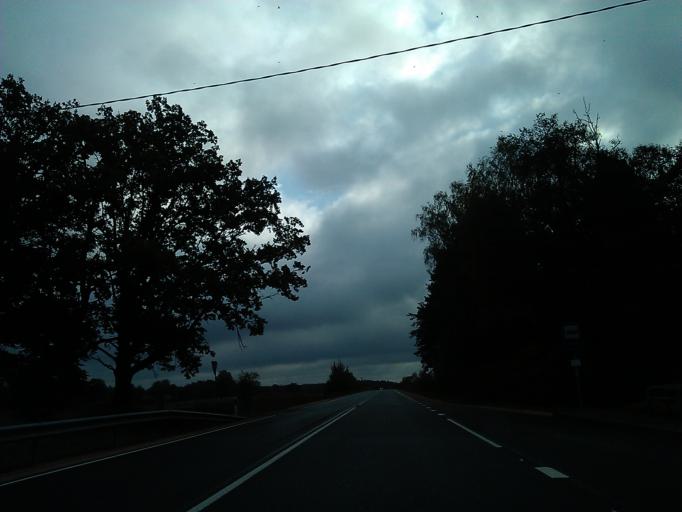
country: LV
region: Salaspils
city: Salaspils
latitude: 56.8993
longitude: 24.4192
